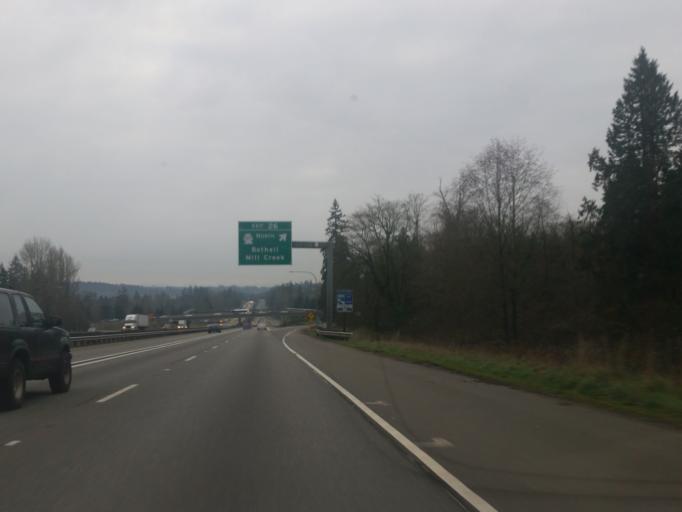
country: US
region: Washington
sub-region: King County
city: Bothell
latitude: 47.7974
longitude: -122.2197
